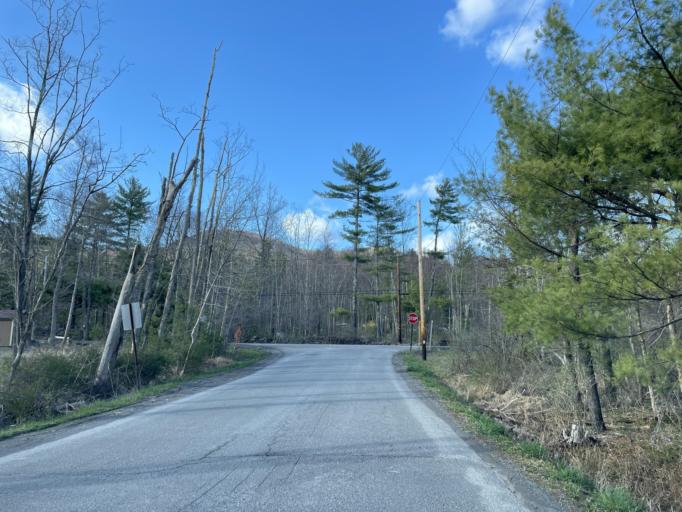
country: US
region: New York
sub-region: Ulster County
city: Woodstock
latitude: 42.0503
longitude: -74.1382
